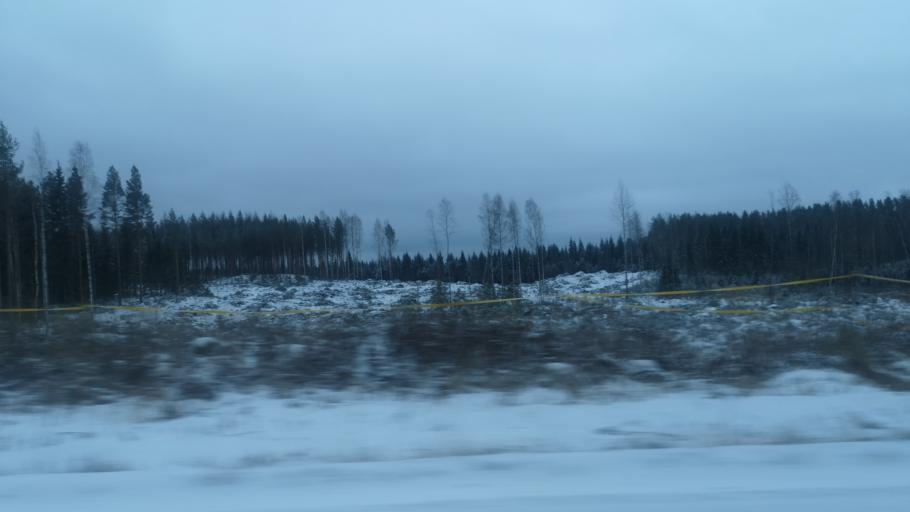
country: FI
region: Southern Savonia
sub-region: Savonlinna
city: Enonkoski
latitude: 62.0921
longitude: 28.6720
